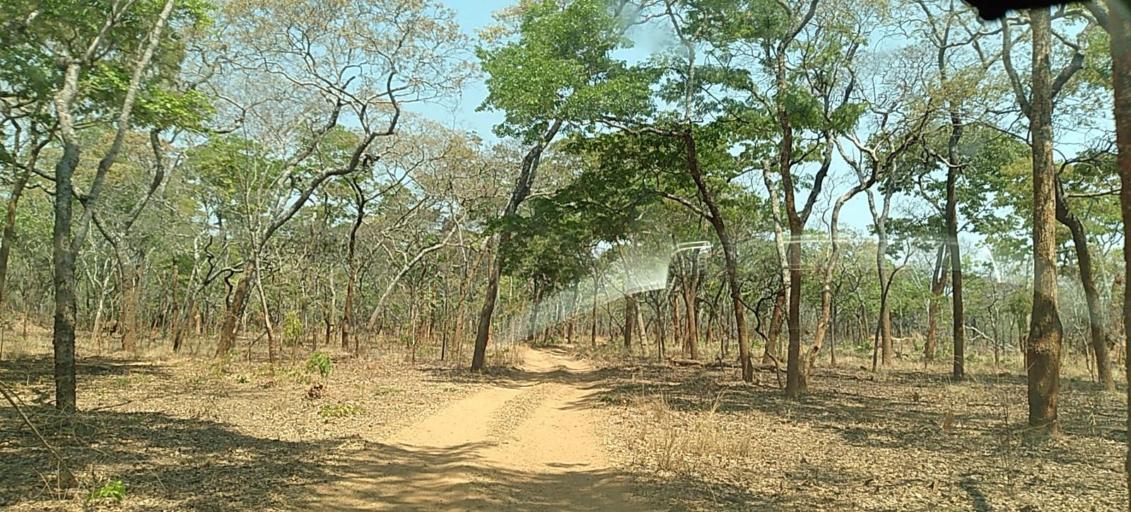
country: ZM
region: North-Western
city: Kasempa
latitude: -13.3942
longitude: 25.5850
